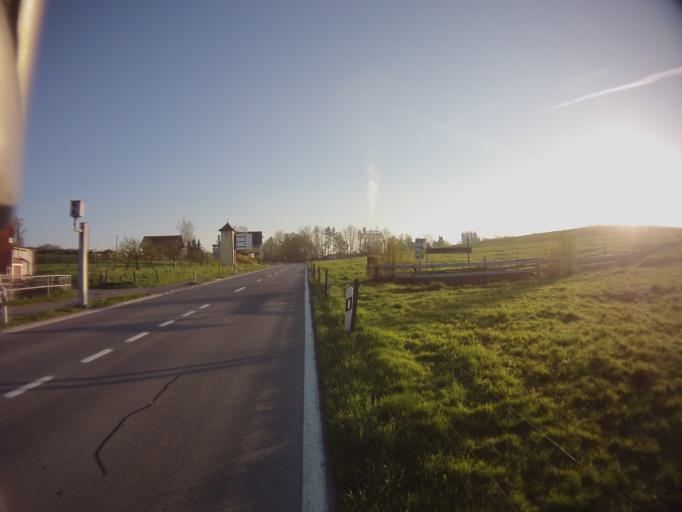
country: CH
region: Zurich
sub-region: Bezirk Affoltern
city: Knonau
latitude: 47.2097
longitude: 8.4603
